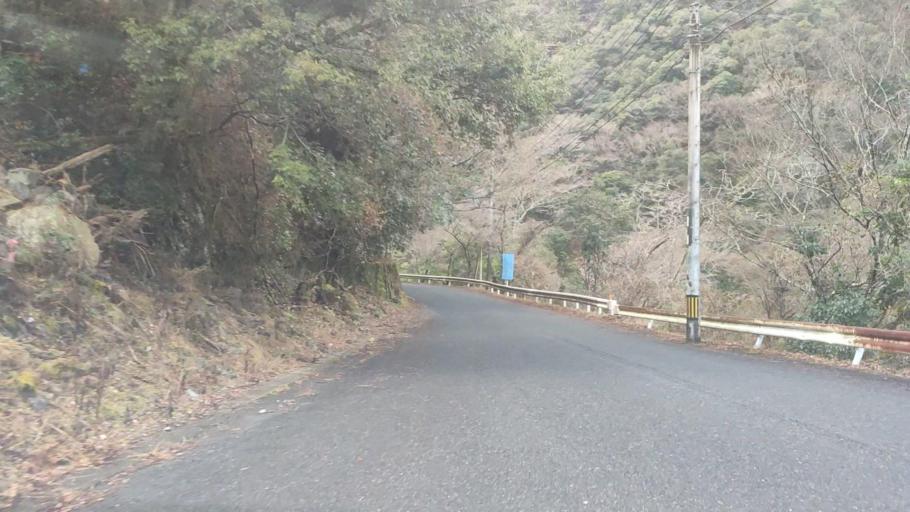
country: JP
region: Kumamoto
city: Matsubase
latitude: 32.4856
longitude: 130.8957
